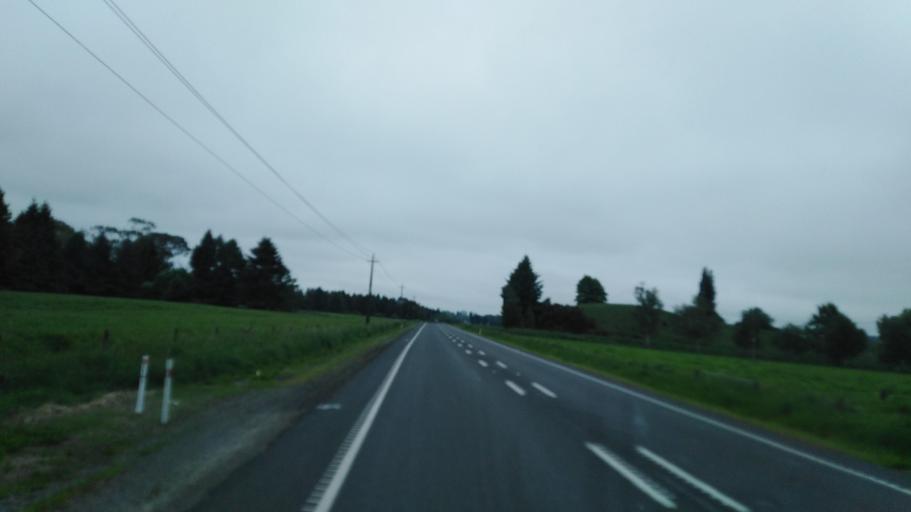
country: NZ
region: Bay of Plenty
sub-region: Rotorua District
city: Rotorua
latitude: -38.3679
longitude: 176.3516
